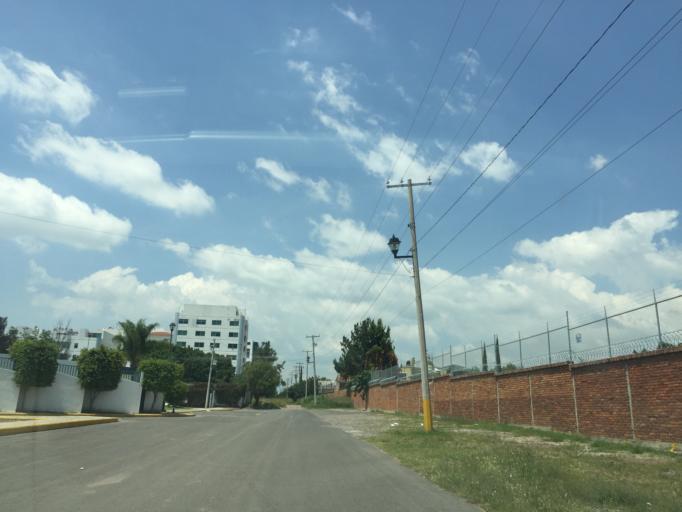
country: MX
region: Guanajuato
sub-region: Leon
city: La Ermita
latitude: 21.1546
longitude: -101.7187
